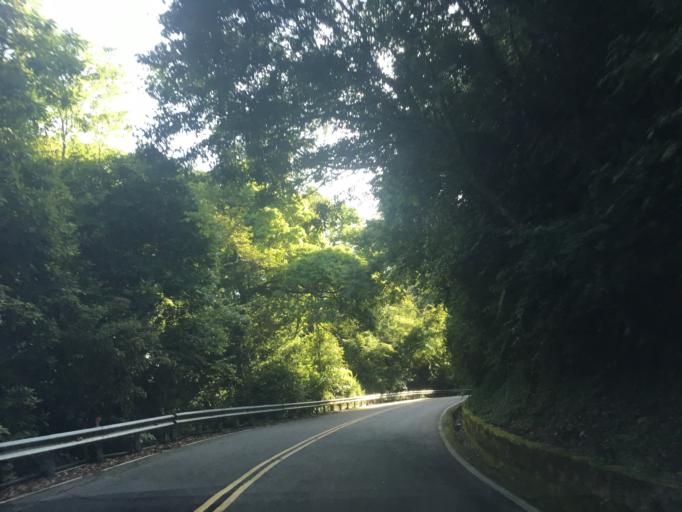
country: TW
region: Taiwan
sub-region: Nantou
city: Puli
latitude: 24.0838
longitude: 121.1697
